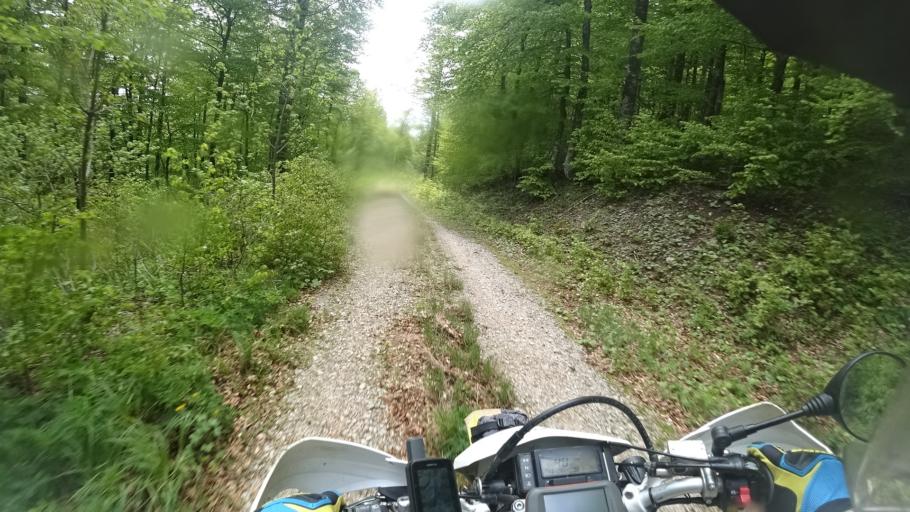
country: BA
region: Federation of Bosnia and Herzegovina
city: Orasac
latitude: 44.5707
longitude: 15.8773
